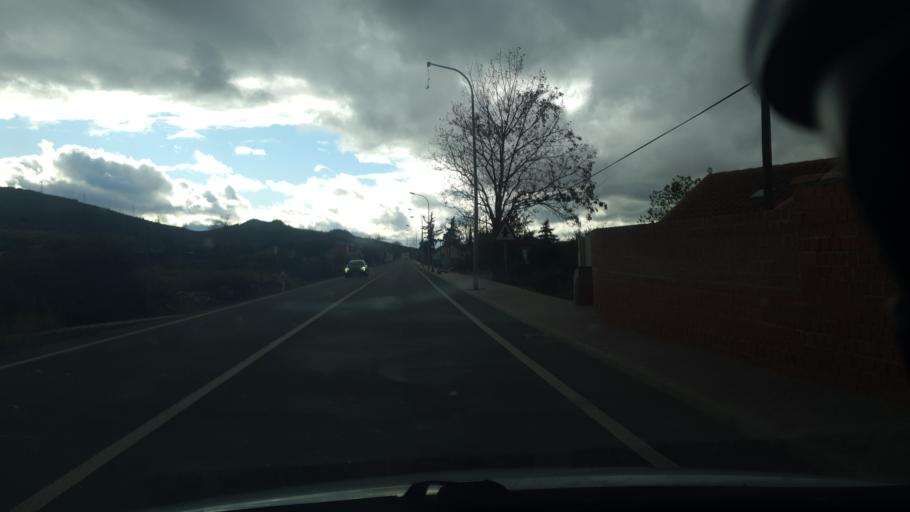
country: ES
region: Castille and Leon
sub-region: Provincia de Avila
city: Ojos-Albos
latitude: 40.7422
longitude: -4.4697
